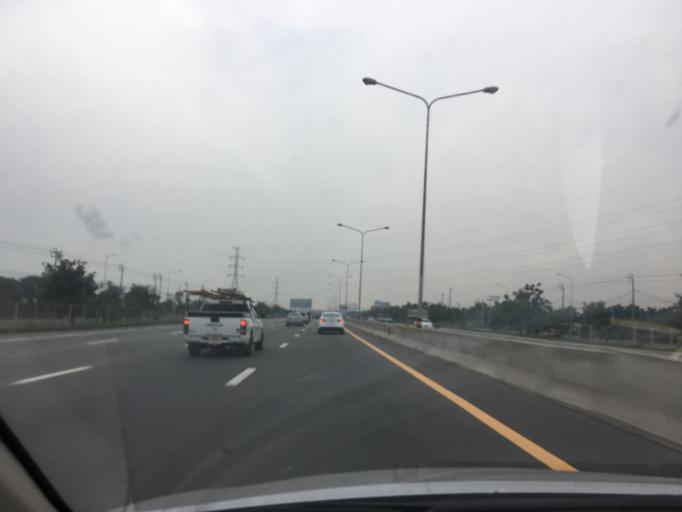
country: TH
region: Bangkok
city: Bang Na
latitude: 13.6780
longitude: 100.6994
